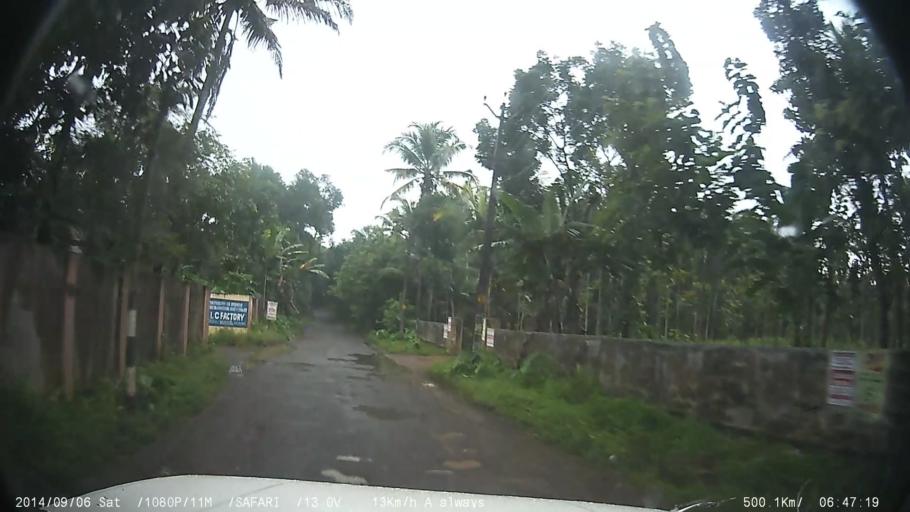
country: IN
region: Kerala
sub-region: Ernakulam
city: Piravam
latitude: 9.7696
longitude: 76.5052
